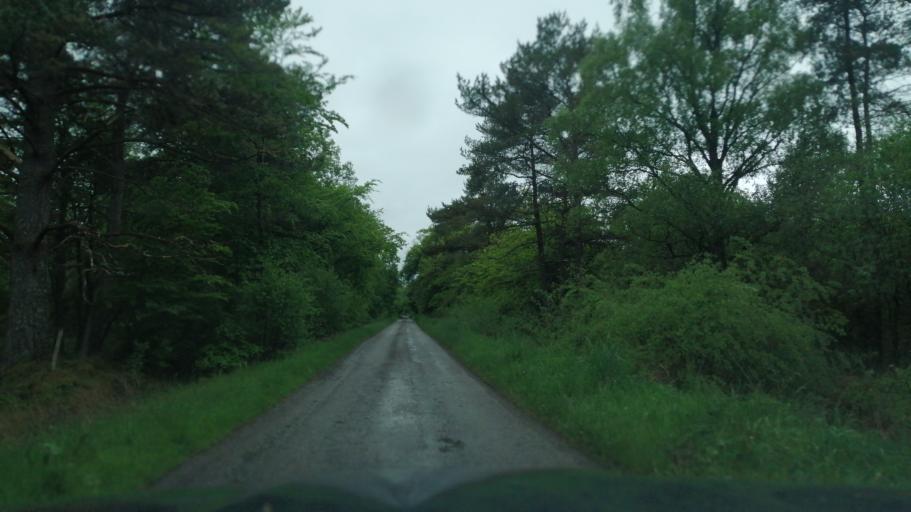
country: GB
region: Scotland
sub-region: Moray
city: Cullen
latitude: 57.5733
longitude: -2.8290
